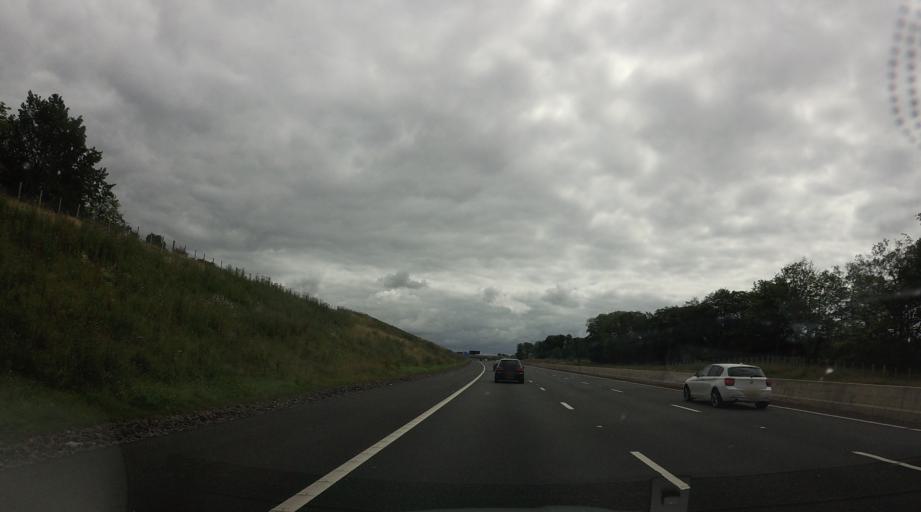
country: GB
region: Scotland
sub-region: North Lanarkshire
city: Coatbridge
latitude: 55.8396
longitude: -4.0370
